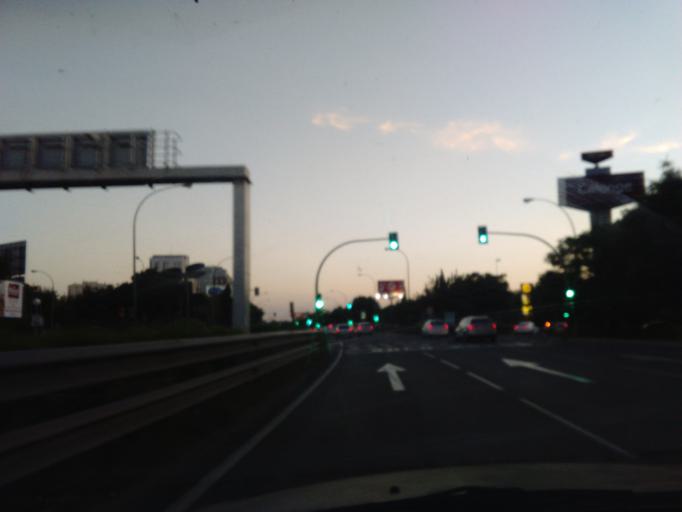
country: ES
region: Andalusia
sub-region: Provincia de Sevilla
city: Sevilla
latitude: 37.4067
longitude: -5.9538
